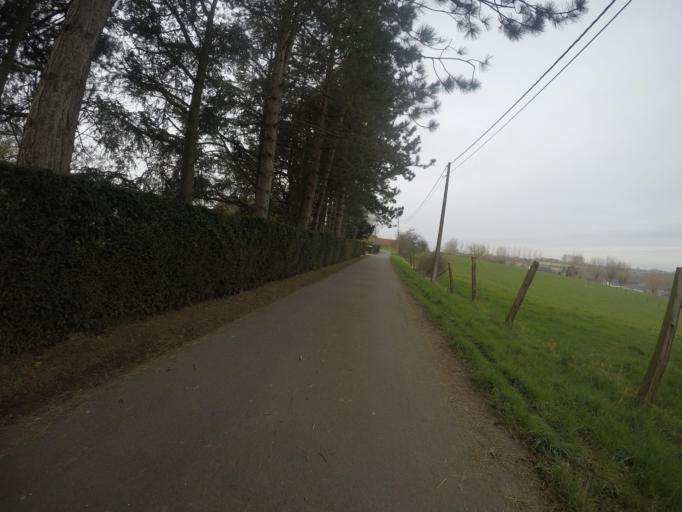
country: BE
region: Flanders
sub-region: Provincie Oost-Vlaanderen
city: Sint-Maria-Lierde
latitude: 50.8148
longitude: 3.8073
